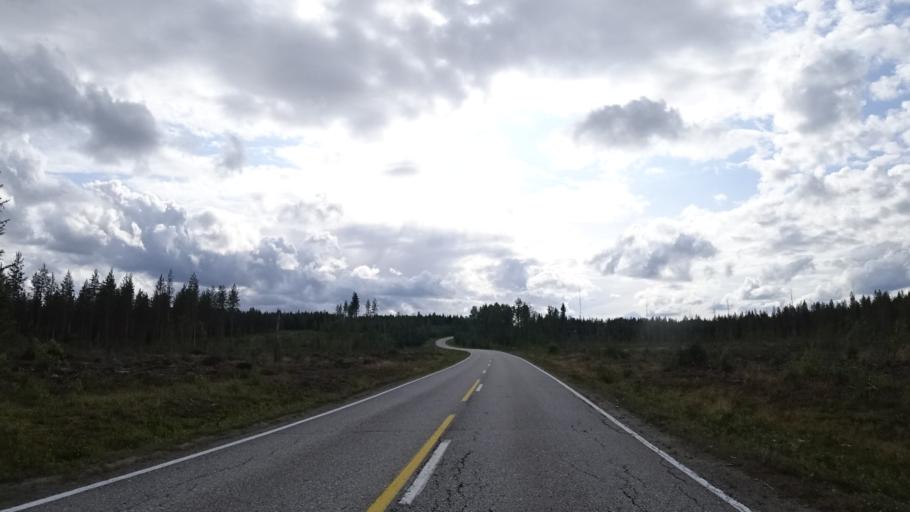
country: FI
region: North Karelia
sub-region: Joensuu
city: Ilomantsi
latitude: 62.7755
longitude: 31.0702
